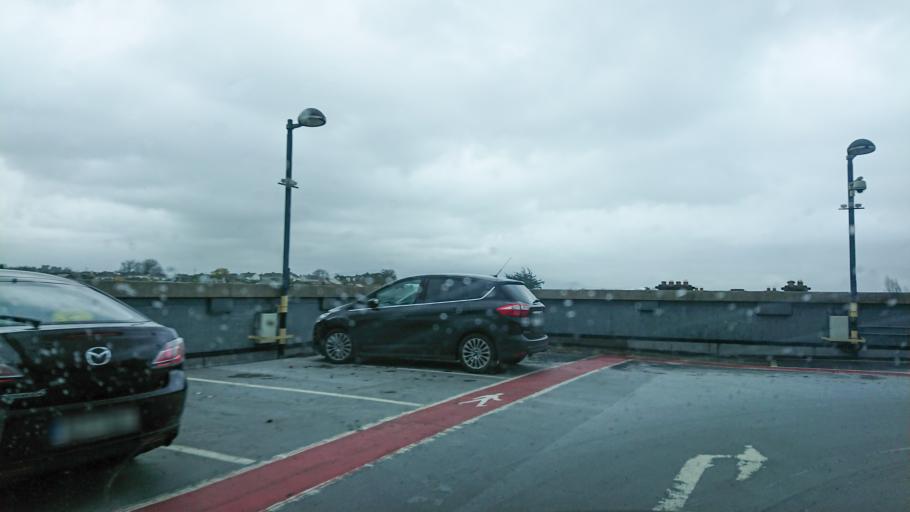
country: IE
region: Munster
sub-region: South Tipperary
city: Cluain Meala
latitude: 52.3553
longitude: -7.6911
